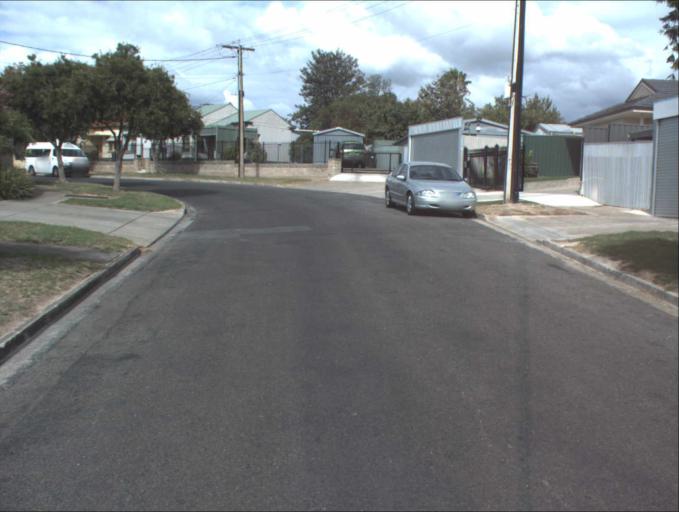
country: AU
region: South Australia
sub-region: Port Adelaide Enfield
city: Blair Athol
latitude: -34.8698
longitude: 138.5930
